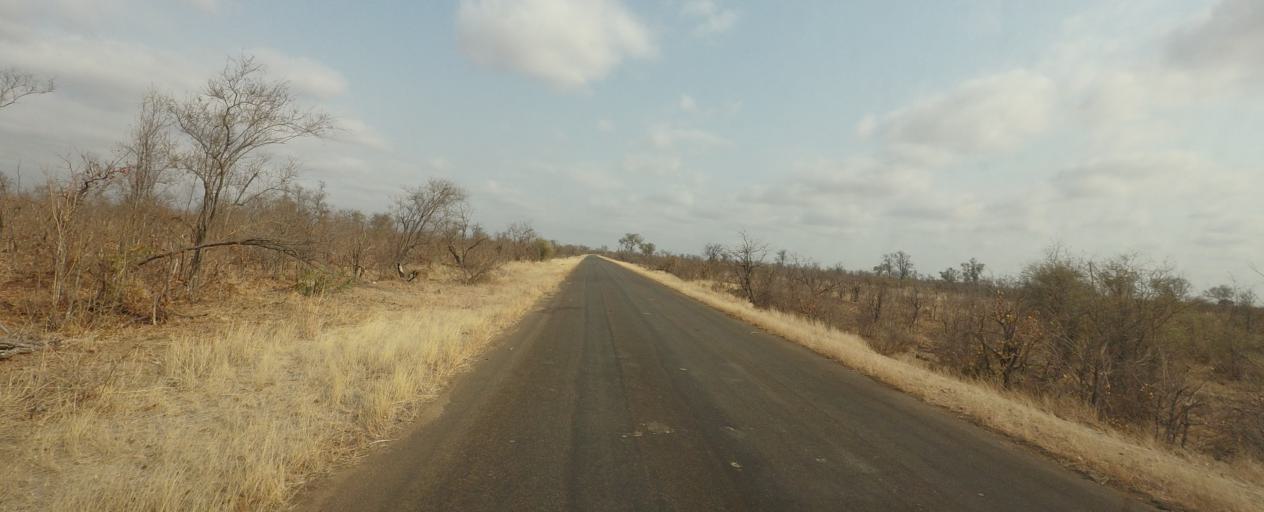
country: ZA
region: Limpopo
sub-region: Vhembe District Municipality
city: Mutale
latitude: -22.8932
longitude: 31.2486
